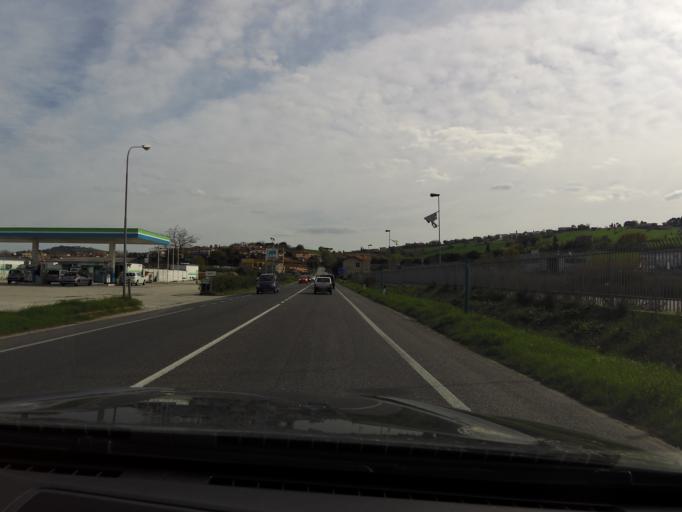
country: IT
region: The Marches
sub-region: Provincia di Ancona
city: Camerano
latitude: 43.5002
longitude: 13.5352
